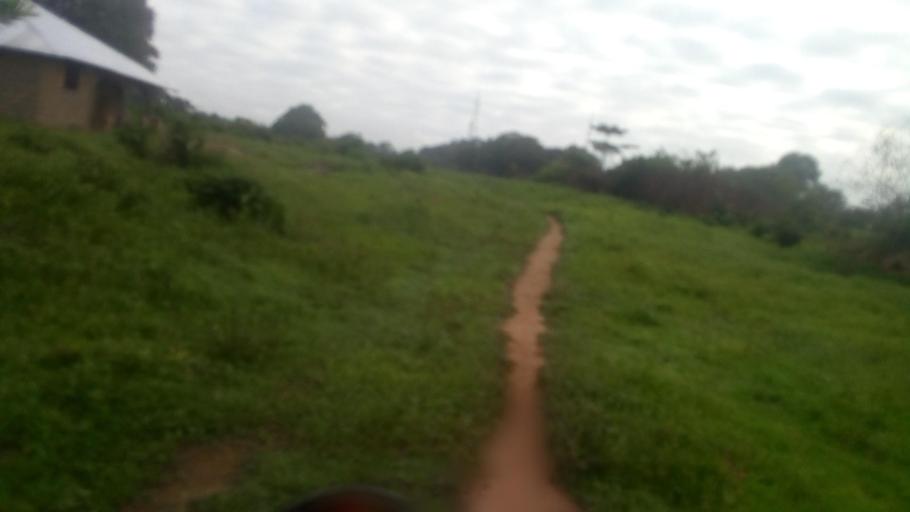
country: SL
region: Eastern Province
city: Pendembu
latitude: 8.0943
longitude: -10.6969
